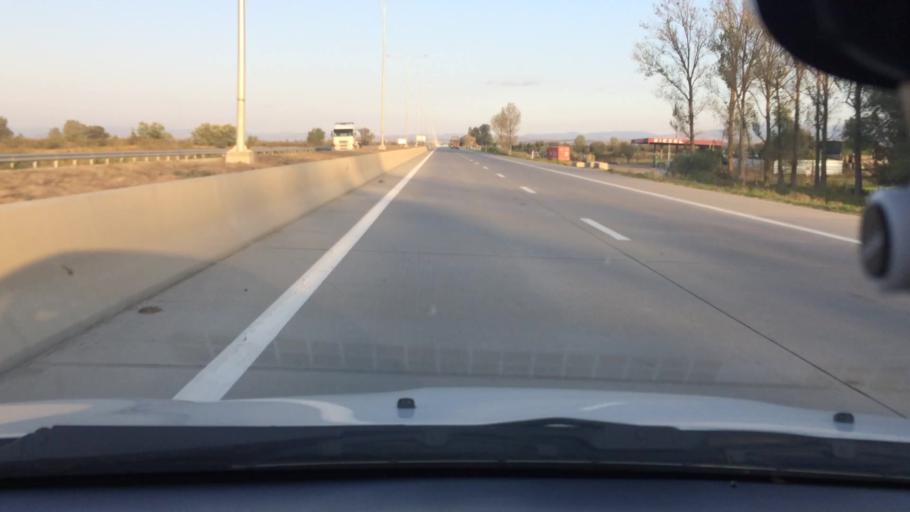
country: GE
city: Agara
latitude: 42.0381
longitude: 43.9352
